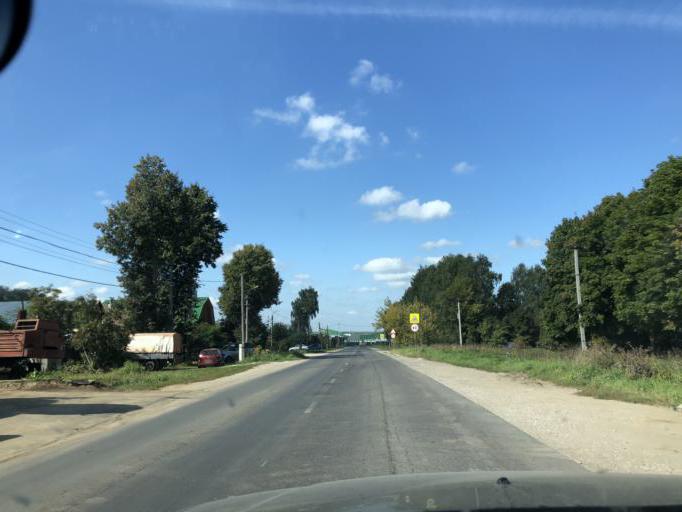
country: RU
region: Tula
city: Yasnogorsk
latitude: 54.4881
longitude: 37.6942
